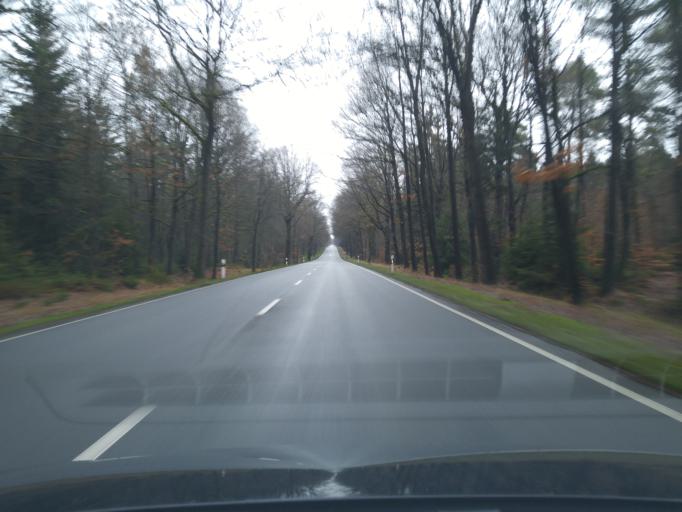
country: DE
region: Lower Saxony
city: Sprakensehl
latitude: 52.7913
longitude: 10.4900
